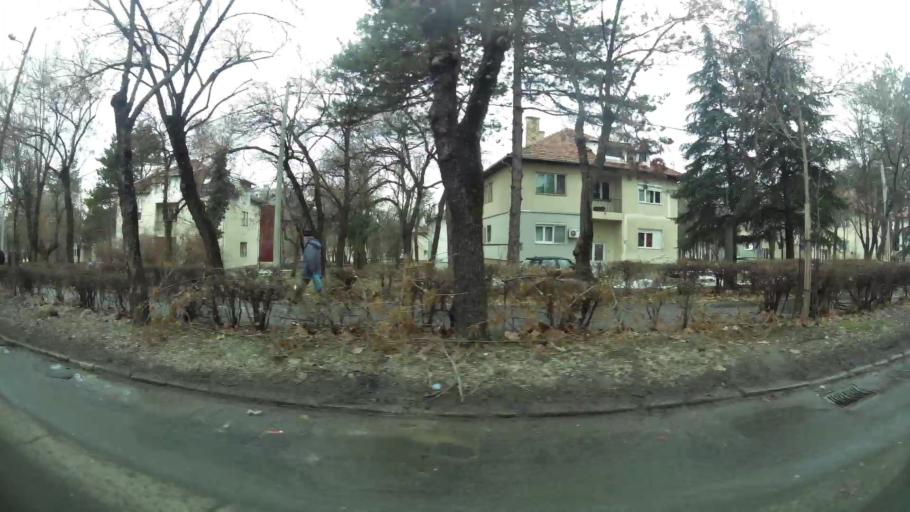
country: RS
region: Central Serbia
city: Sremcica
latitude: 44.7282
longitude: 20.3747
